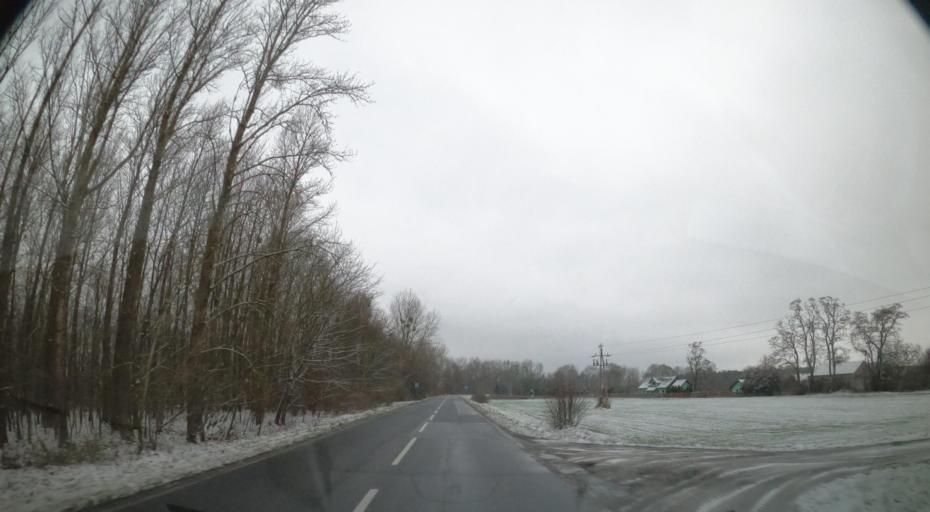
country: PL
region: Masovian Voivodeship
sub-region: Powiat plocki
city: Nowy Duninow
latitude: 52.5791
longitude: 19.5377
